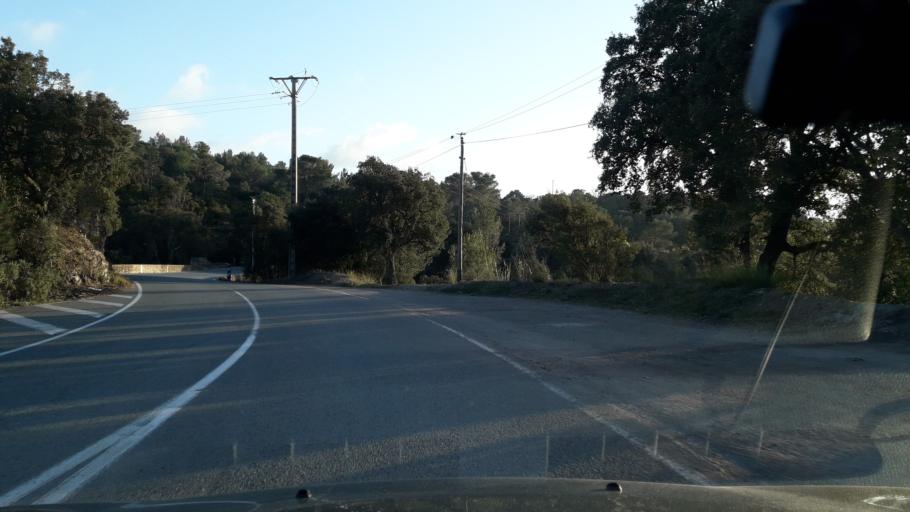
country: FR
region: Provence-Alpes-Cote d'Azur
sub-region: Departement du Var
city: Saint-Raphael
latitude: 43.4734
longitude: 6.7690
